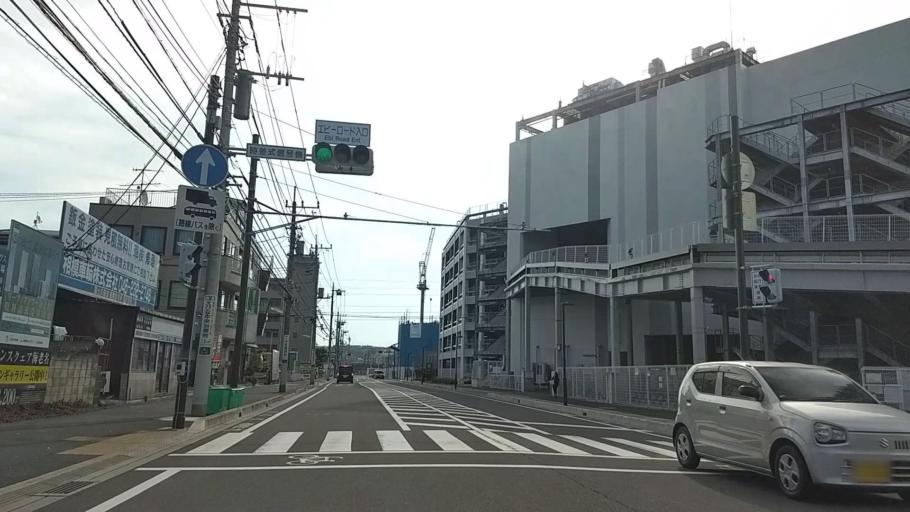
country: JP
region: Kanagawa
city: Zama
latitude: 35.4576
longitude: 139.3888
